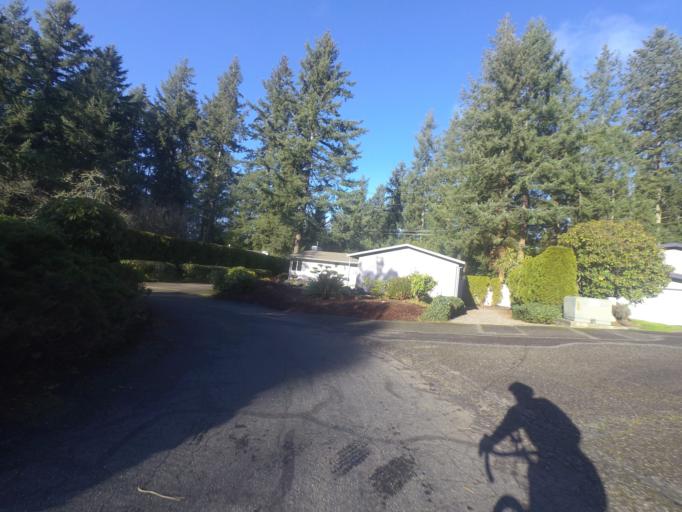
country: US
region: Washington
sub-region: Pierce County
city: University Place
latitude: 47.2130
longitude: -122.5640
